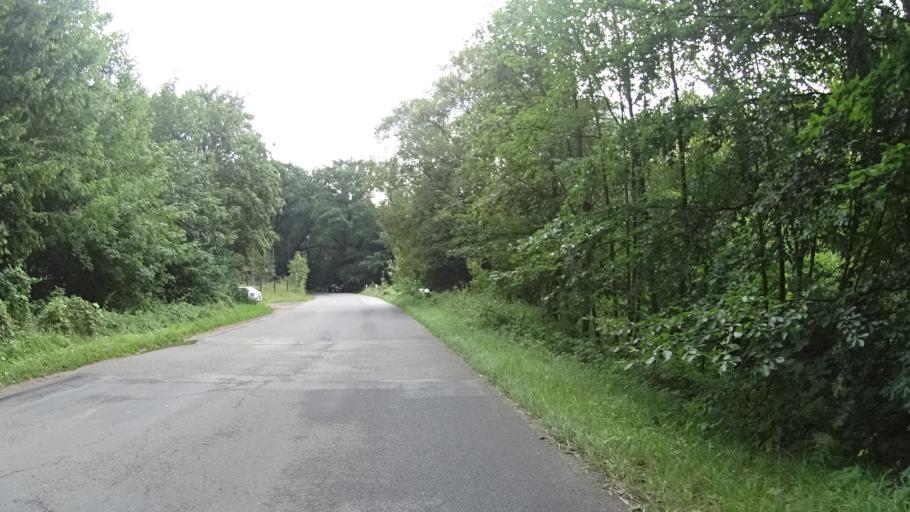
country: DE
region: Hamburg
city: Duvenstedt
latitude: 53.7204
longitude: 10.1159
